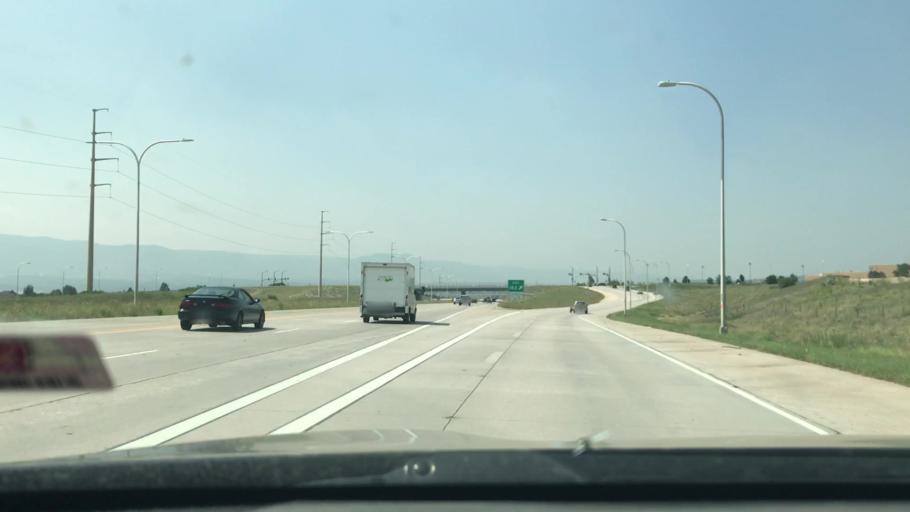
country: US
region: Colorado
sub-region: El Paso County
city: Black Forest
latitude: 38.9818
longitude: -104.7603
